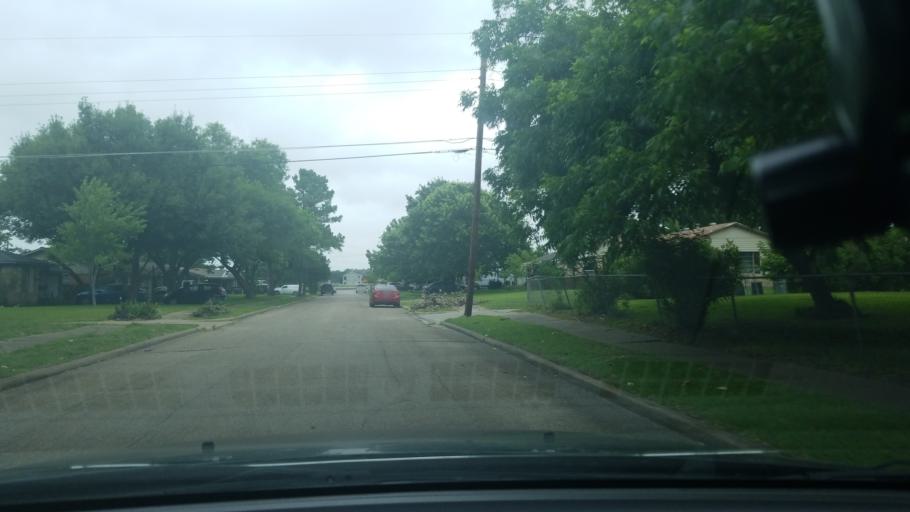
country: US
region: Texas
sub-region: Dallas County
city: Mesquite
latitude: 32.7898
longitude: -96.6370
